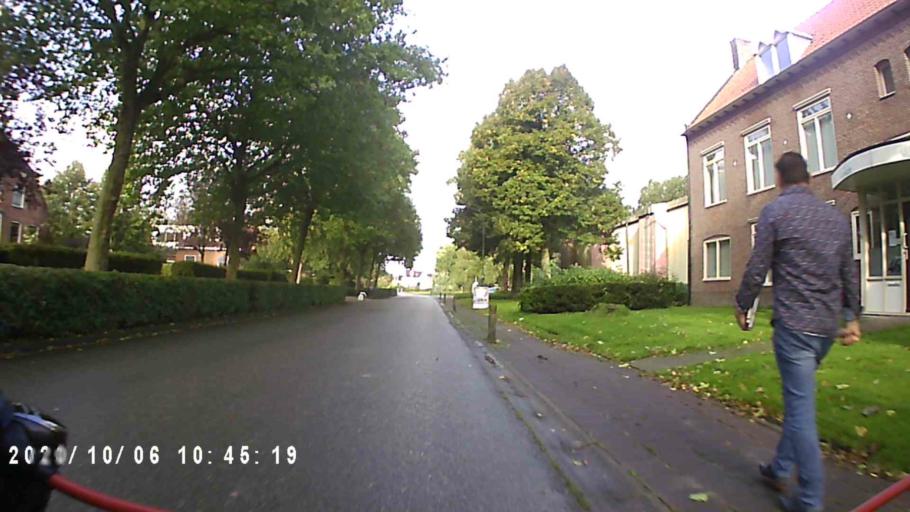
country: NL
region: Groningen
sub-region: Gemeente Zuidhorn
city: Oldehove
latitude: 53.3588
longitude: 6.4260
